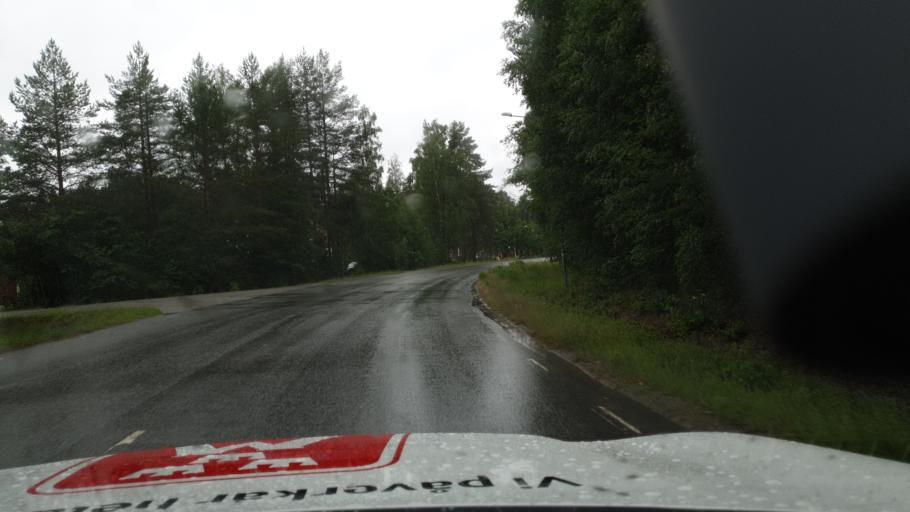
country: SE
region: Vaesterbotten
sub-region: Nordmalings Kommun
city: Nordmaling
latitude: 63.5475
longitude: 19.4043
